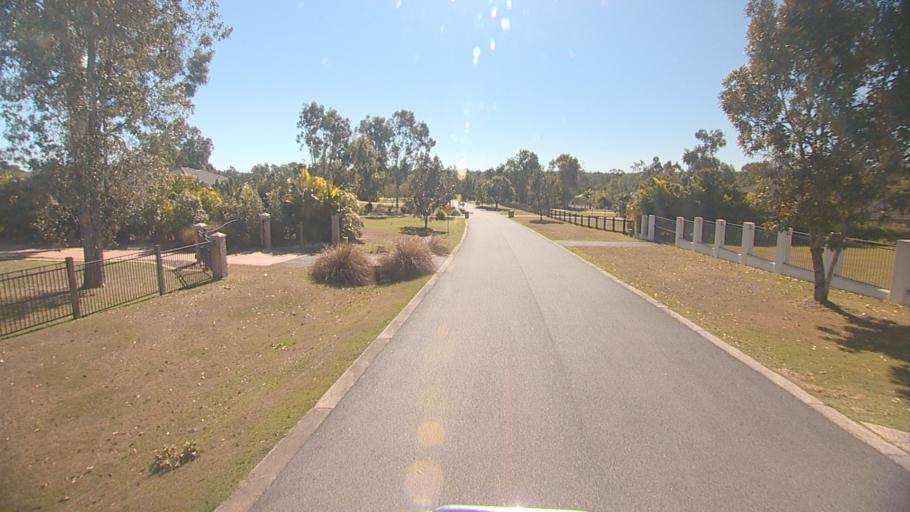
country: AU
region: Queensland
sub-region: Logan
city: North Maclean
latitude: -27.7587
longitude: 152.9643
